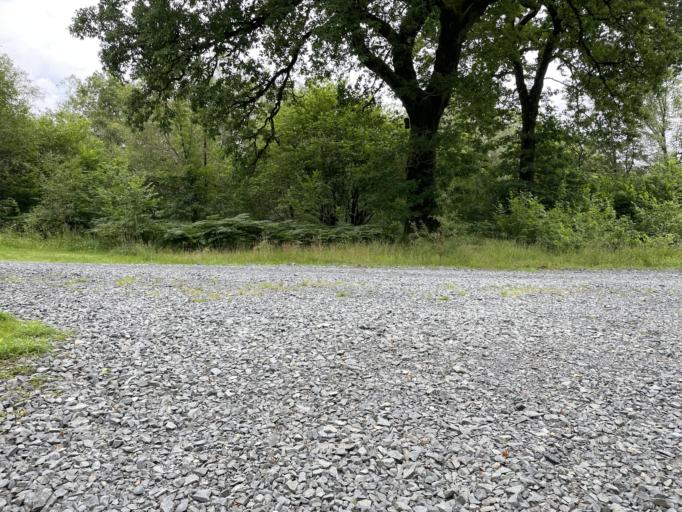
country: GB
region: Scotland
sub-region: Dumfries and Galloway
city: Newton Stewart
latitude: 55.0796
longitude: -4.5121
